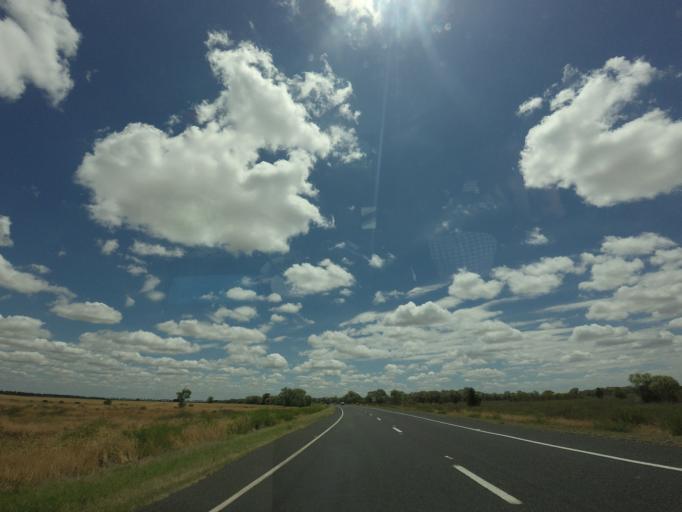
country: AU
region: New South Wales
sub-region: Moree Plains
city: Boggabilla
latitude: -28.9945
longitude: 150.0739
